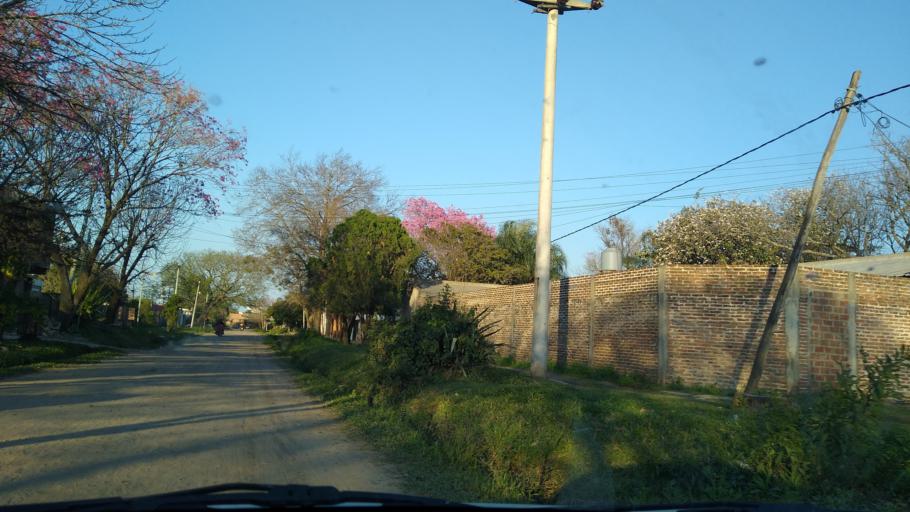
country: AR
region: Chaco
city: Barranqueras
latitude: -27.4694
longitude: -58.9572
